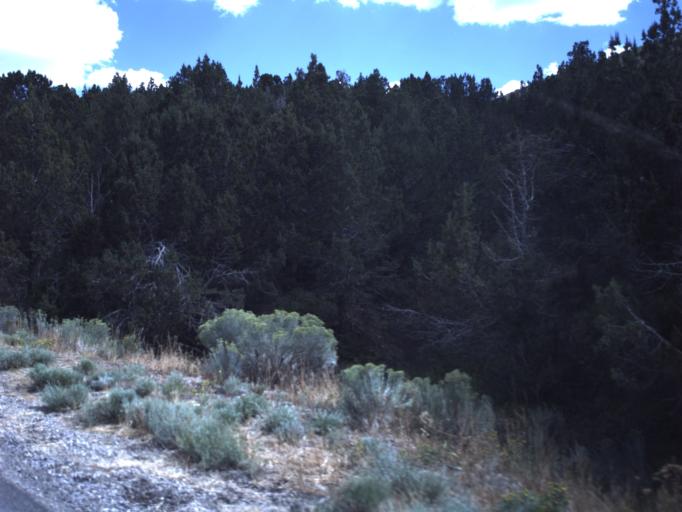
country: US
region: Utah
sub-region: Tooele County
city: Grantsville
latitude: 40.3429
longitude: -112.5813
